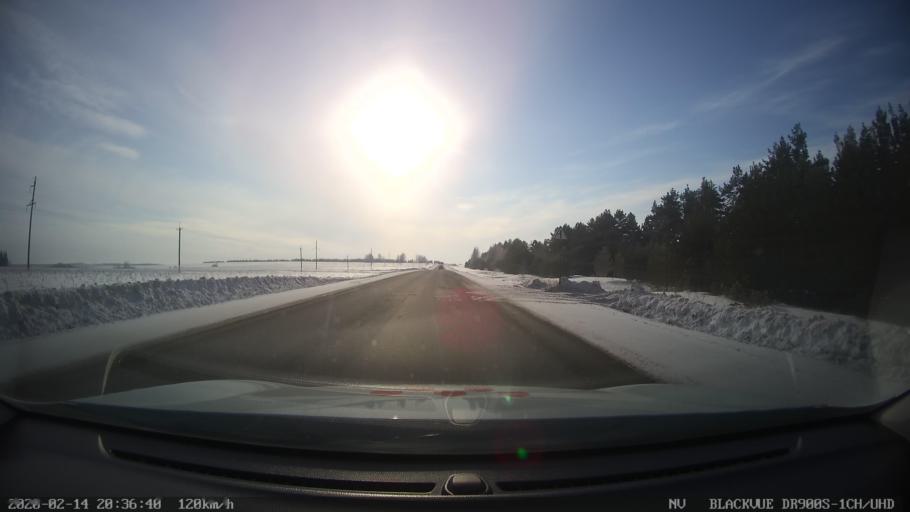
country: RU
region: Tatarstan
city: Kuybyshevskiy Zaton
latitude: 55.3636
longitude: 49.0015
